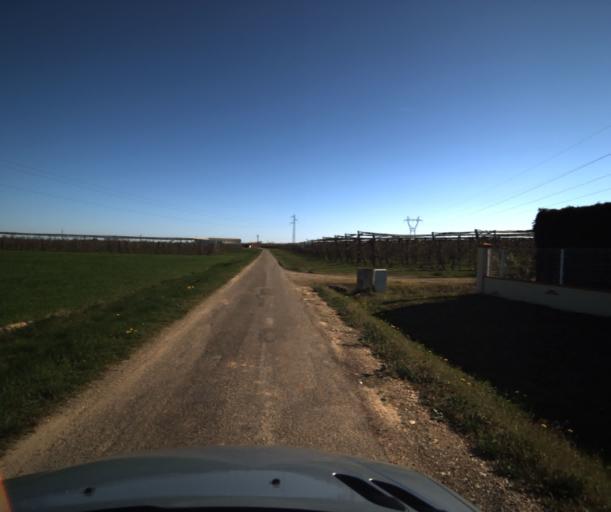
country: FR
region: Midi-Pyrenees
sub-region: Departement du Tarn-et-Garonne
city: Bressols
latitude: 43.9436
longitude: 1.3292
